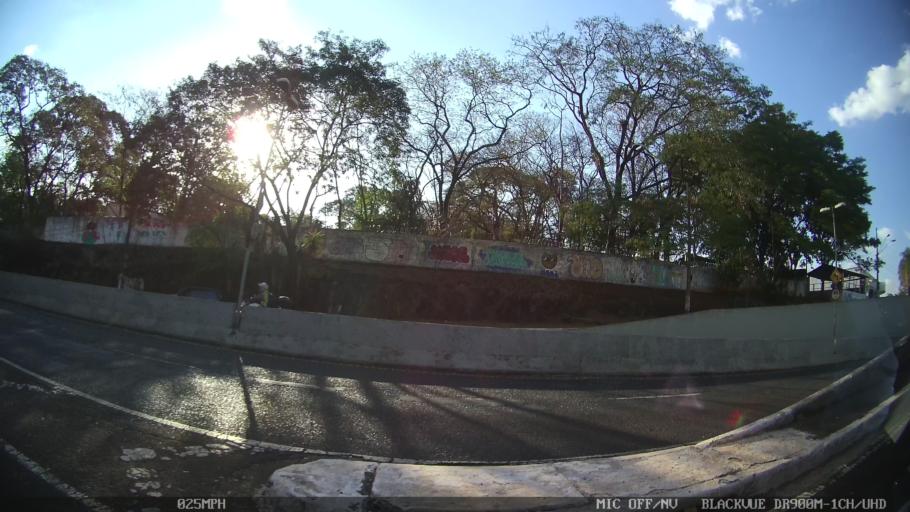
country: BR
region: Sao Paulo
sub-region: Ribeirao Preto
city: Ribeirao Preto
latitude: -21.1755
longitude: -47.7959
